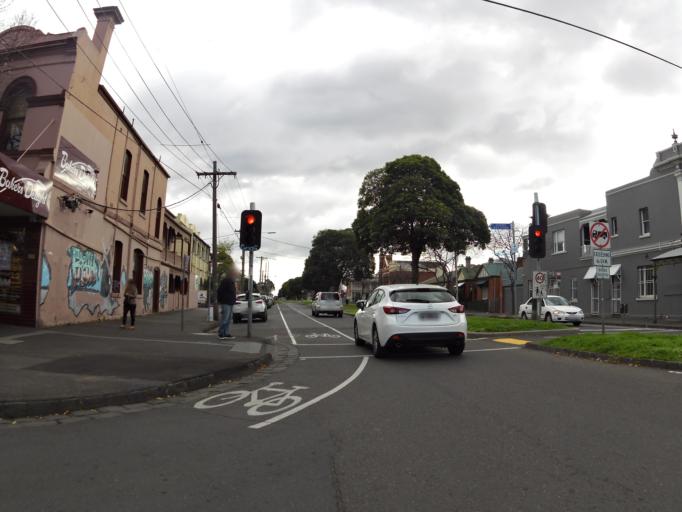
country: AU
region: Victoria
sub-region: Yarra
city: Clifton Hill
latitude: -37.7886
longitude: 144.9908
